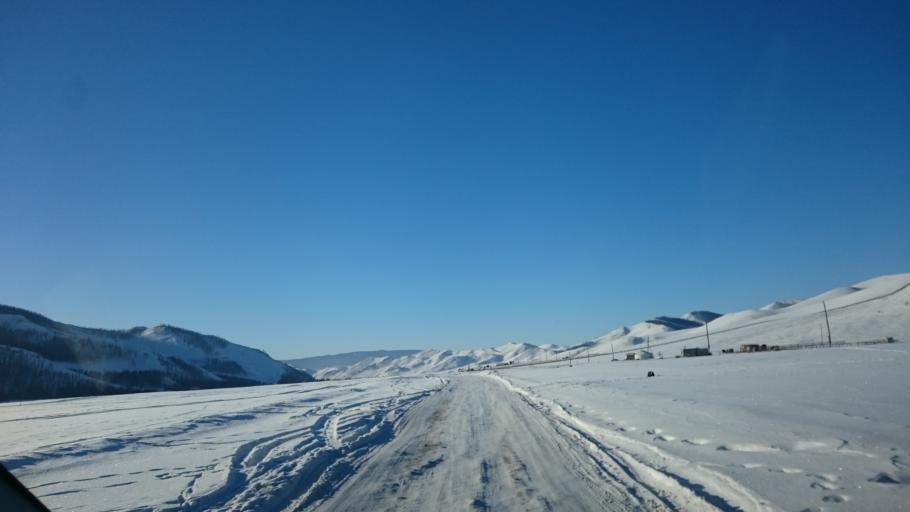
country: MN
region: Ulaanbaatar
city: Ulaanbaatar
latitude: 48.0061
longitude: 107.2012
